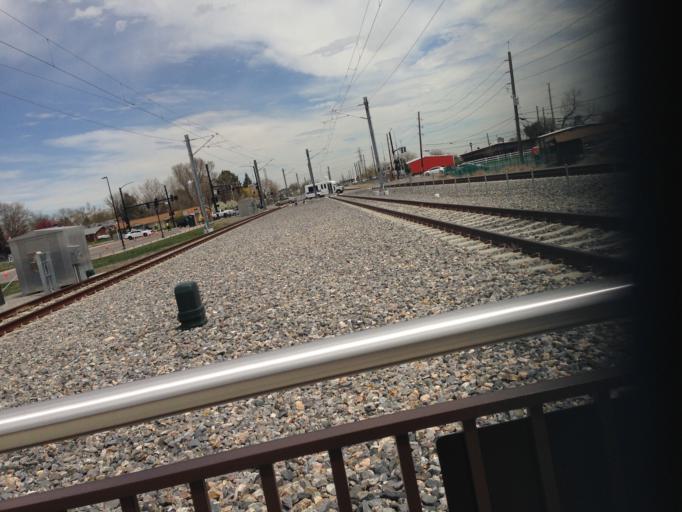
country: US
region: Colorado
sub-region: Jefferson County
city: Applewood
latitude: 39.7882
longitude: -105.1324
